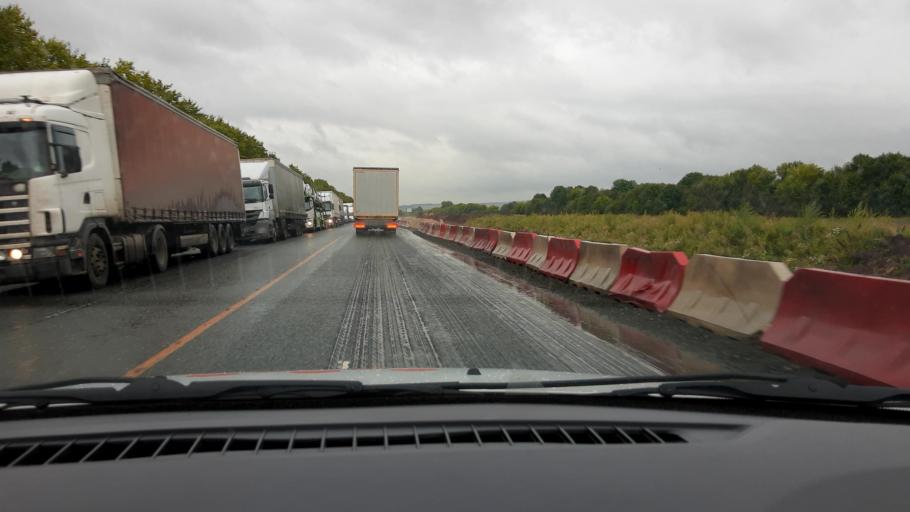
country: RU
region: Chuvashia
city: Yantikovo
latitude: 55.8035
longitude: 47.9048
